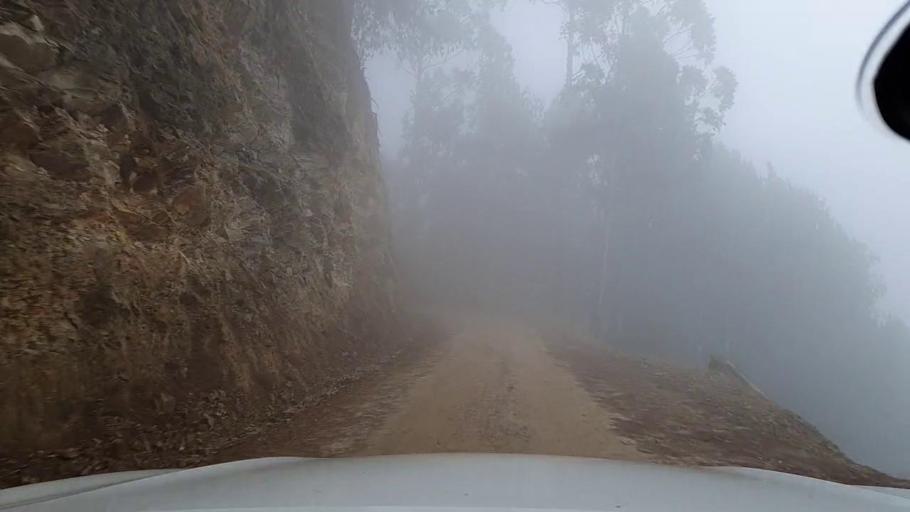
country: BI
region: Cibitoke
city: Cibitoke
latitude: -2.5939
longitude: 29.1925
